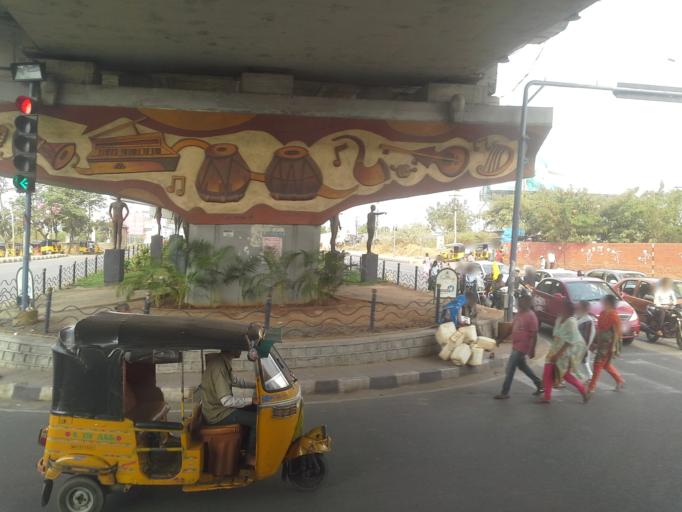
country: IN
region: Telangana
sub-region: Rangareddi
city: Kukatpalli
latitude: 17.4516
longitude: 78.3812
